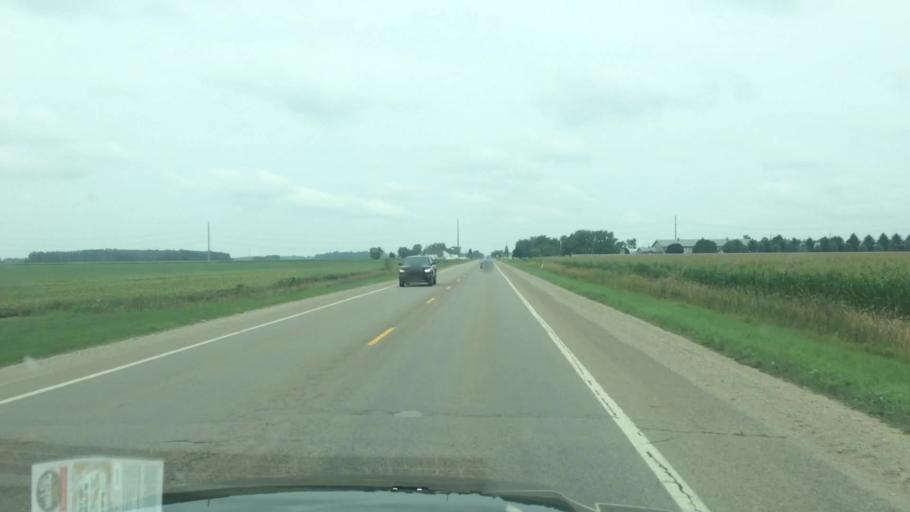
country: US
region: Michigan
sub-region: Huron County
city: Bad Axe
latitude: 43.8327
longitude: -83.0013
